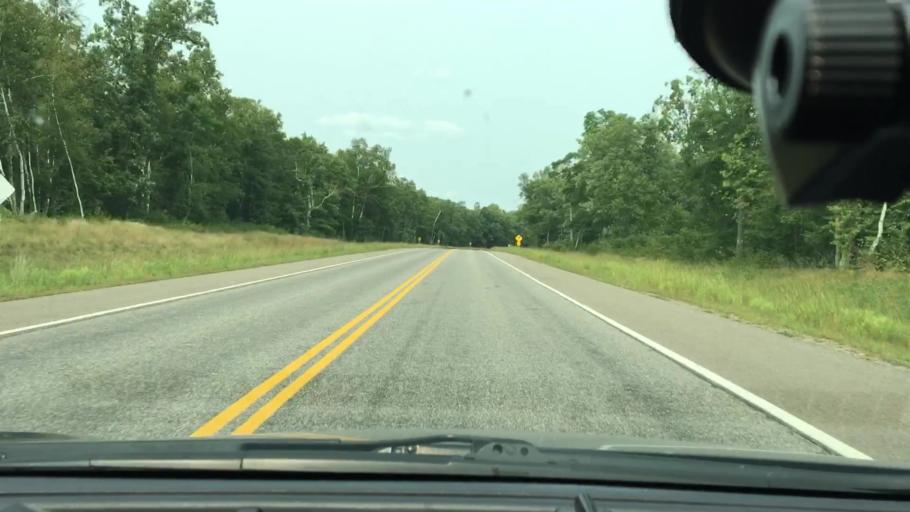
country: US
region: Minnesota
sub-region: Crow Wing County
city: Cross Lake
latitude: 46.6977
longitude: -94.0663
